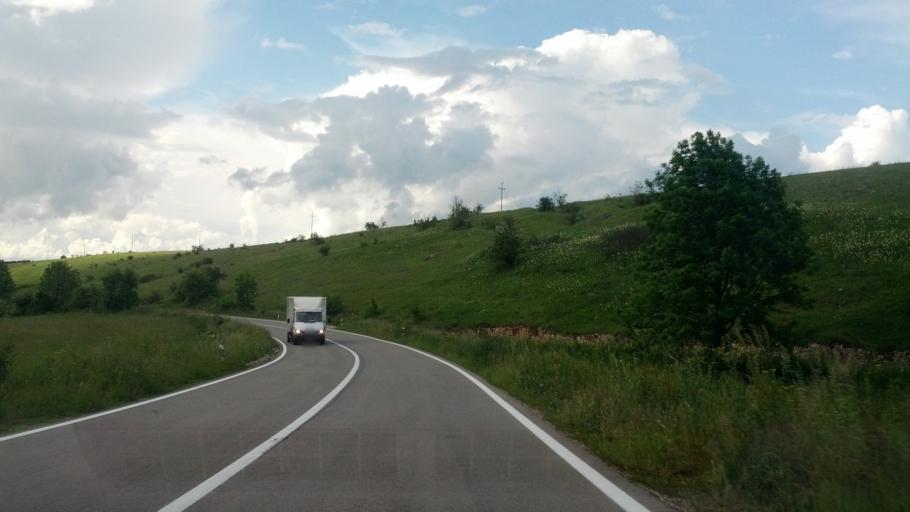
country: BA
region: Federation of Bosnia and Herzegovina
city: Izacic
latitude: 44.9132
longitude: 15.7188
